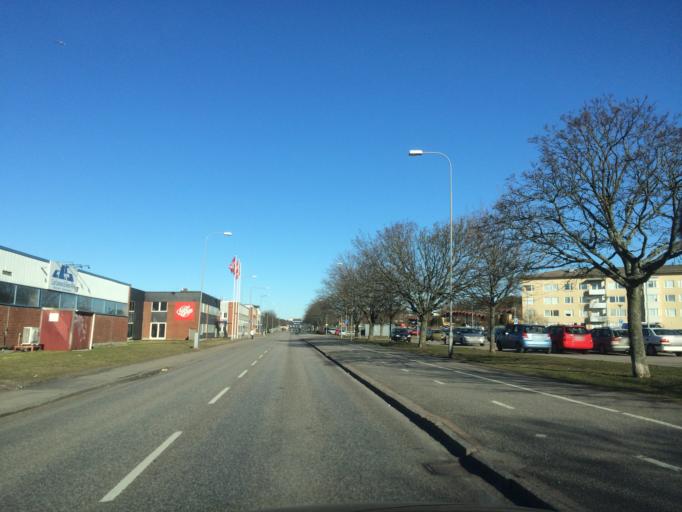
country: SE
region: Vaestra Goetaland
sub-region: Goteborg
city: Majorna
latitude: 57.6556
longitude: 11.9021
